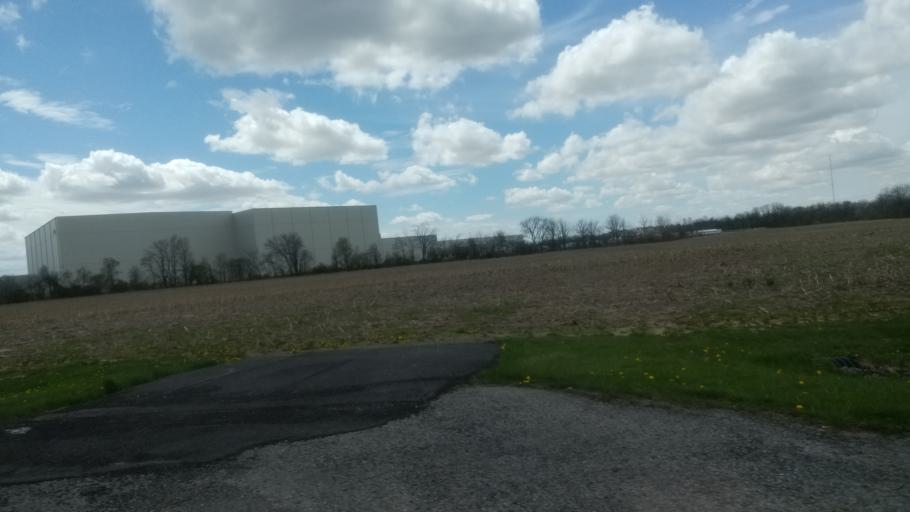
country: US
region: Ohio
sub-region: Hancock County
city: Findlay
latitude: 41.0825
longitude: -83.6324
